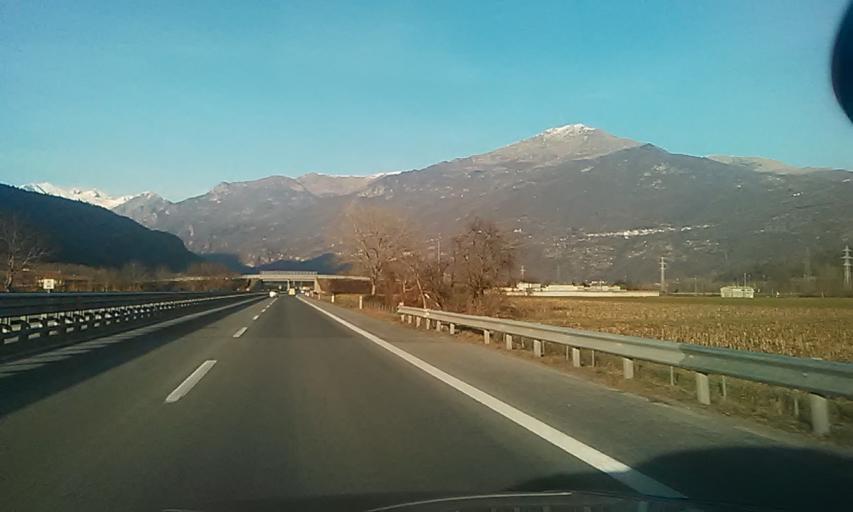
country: IT
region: Piedmont
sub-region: Provincia di Torino
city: Quassolo
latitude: 45.5051
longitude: 7.8321
